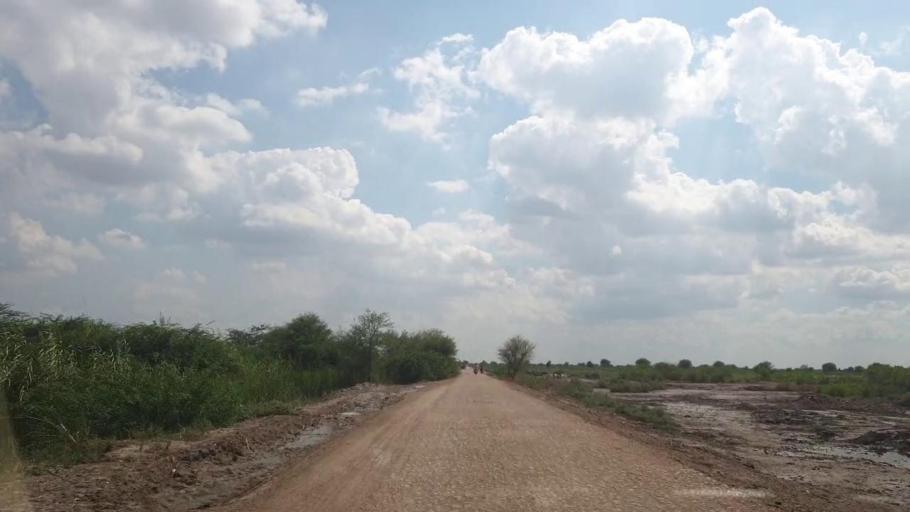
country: PK
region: Sindh
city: Pithoro
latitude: 25.5845
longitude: 69.3909
